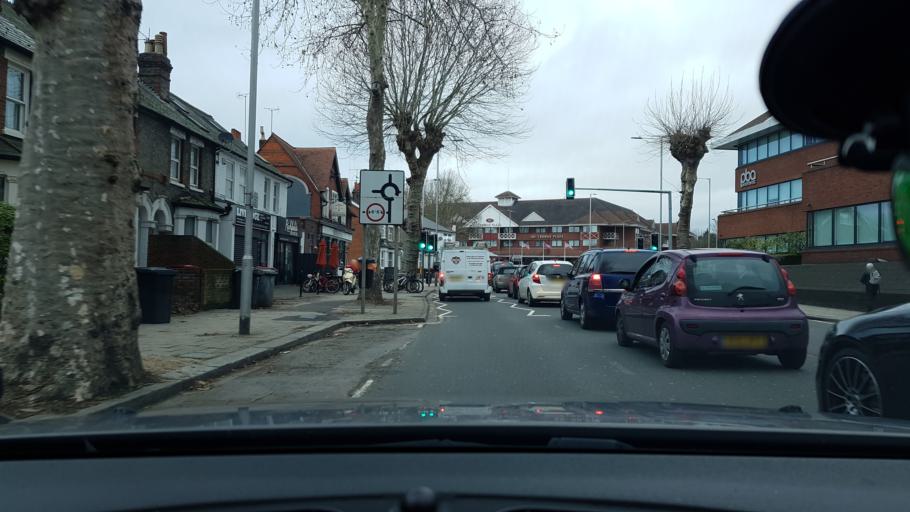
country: GB
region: England
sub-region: Reading
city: Reading
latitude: 51.4639
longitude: -0.9768
